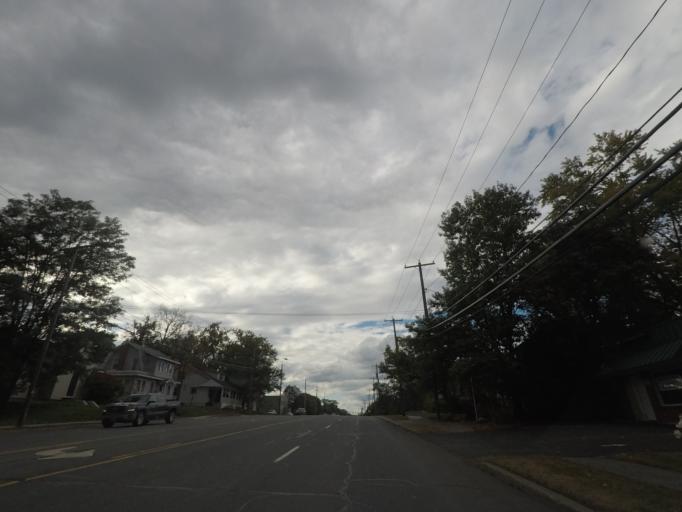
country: US
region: New York
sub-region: Albany County
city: McKownville
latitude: 42.6871
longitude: -73.8563
